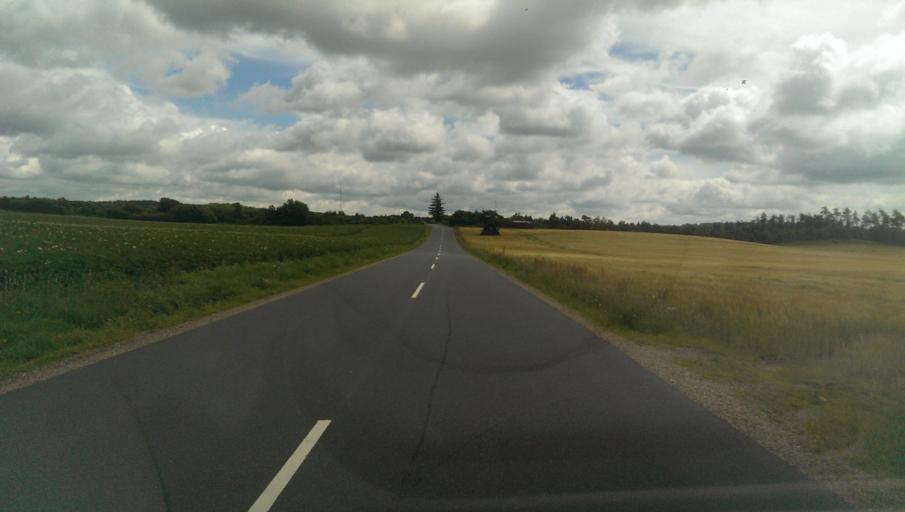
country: DK
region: Central Jutland
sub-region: Silkeborg Kommune
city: Virklund
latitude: 56.0913
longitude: 9.4537
